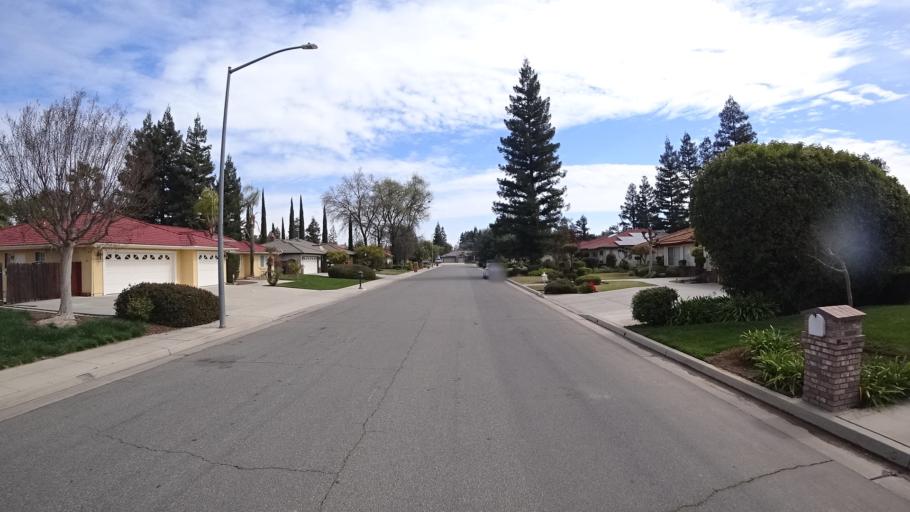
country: US
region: California
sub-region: Fresno County
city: West Park
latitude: 36.8419
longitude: -119.8858
